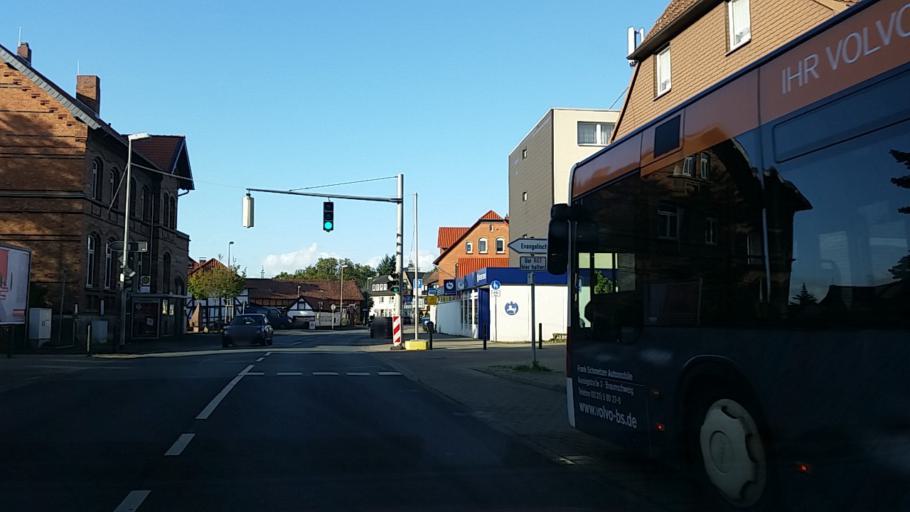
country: DE
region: Lower Saxony
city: Braunschweig
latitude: 52.2923
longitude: 10.5607
